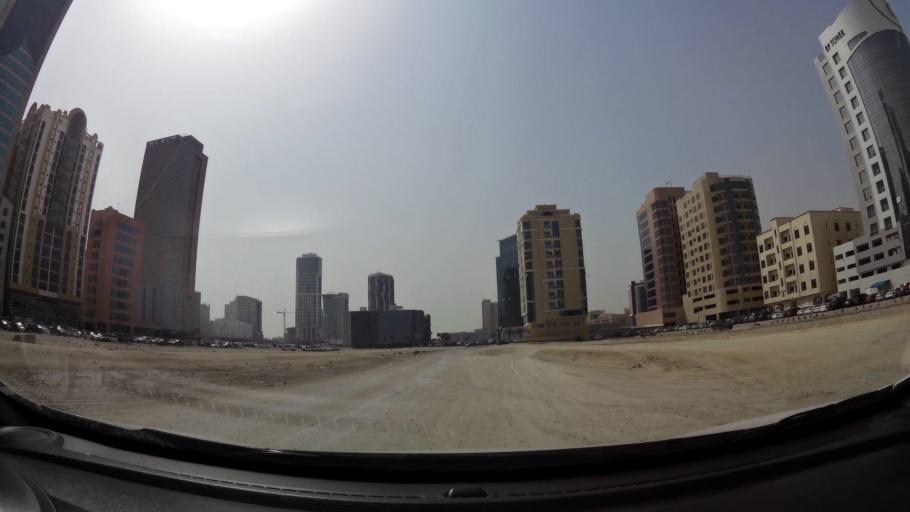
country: BH
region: Manama
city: Jidd Hafs
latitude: 26.2410
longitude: 50.5348
